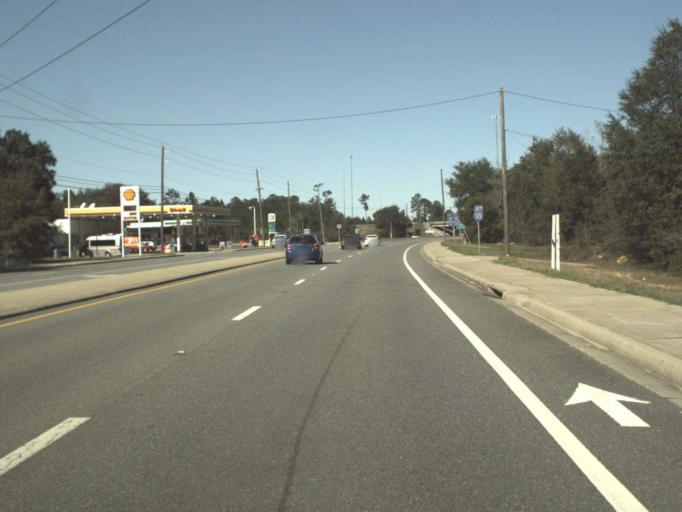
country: US
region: Florida
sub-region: Santa Rosa County
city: East Milton
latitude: 30.6154
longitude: -86.9605
